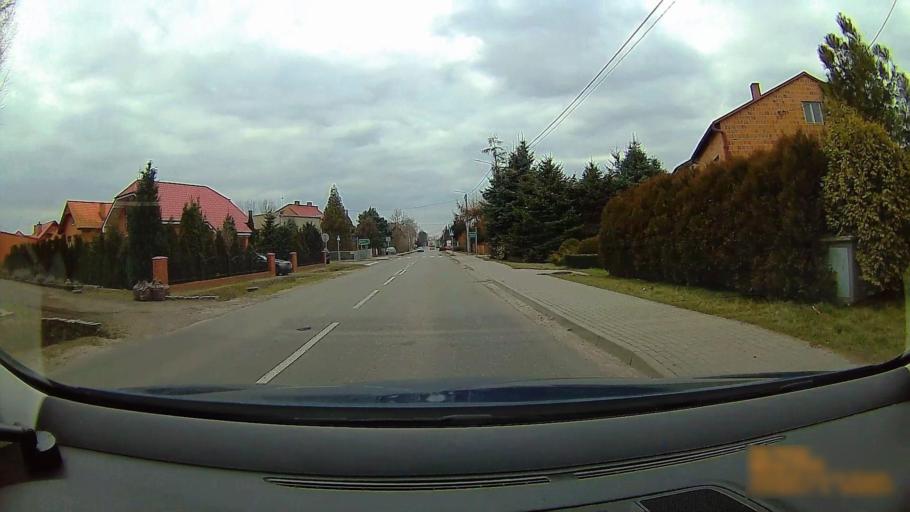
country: PL
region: Greater Poland Voivodeship
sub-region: Powiat koninski
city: Rzgow Pierwszy
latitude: 52.1569
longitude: 18.0563
